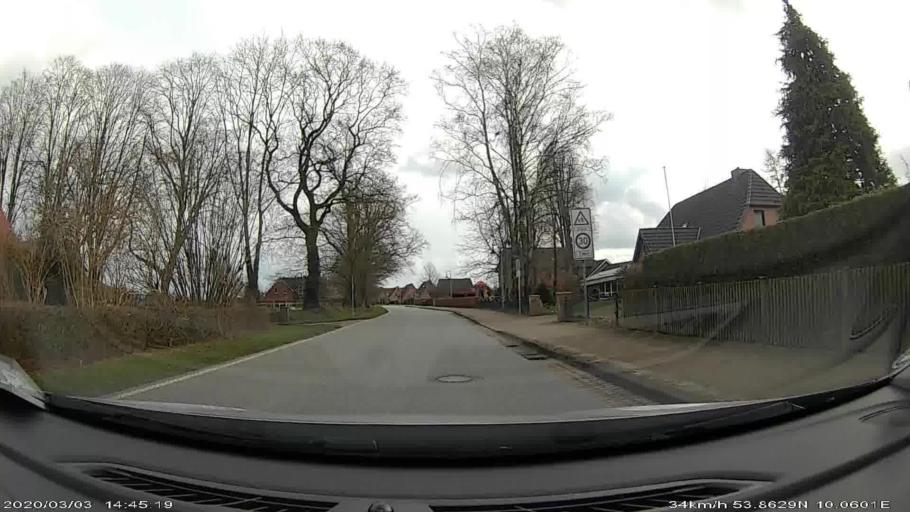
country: DE
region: Schleswig-Holstein
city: Struvenhutten
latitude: 53.8630
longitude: 10.0604
